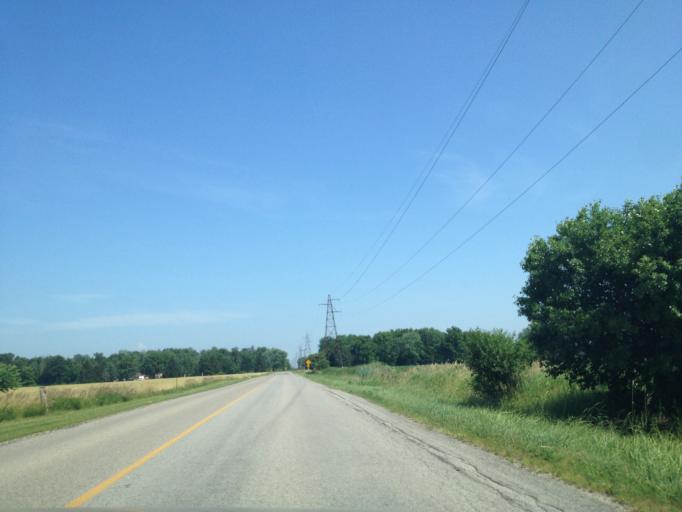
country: CA
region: Ontario
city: London
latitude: 43.0766
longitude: -81.2122
